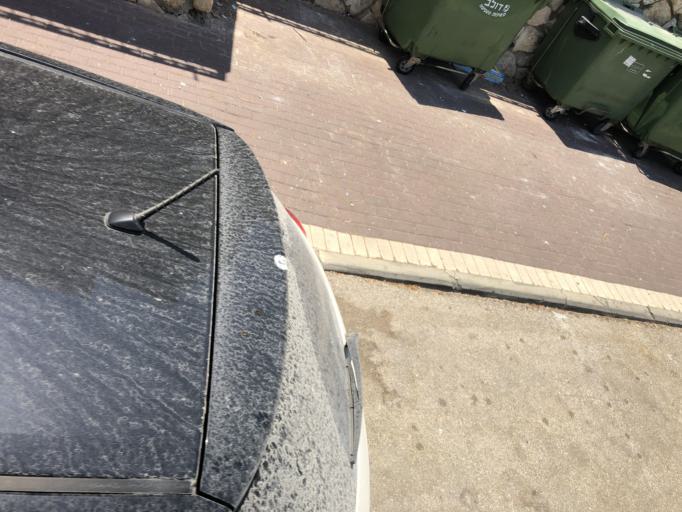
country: IL
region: Haifa
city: Daliyat el Karmil
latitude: 32.6395
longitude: 35.0915
